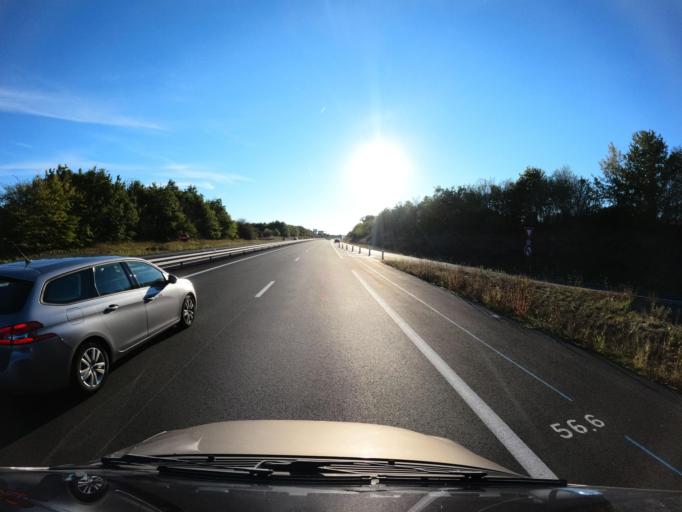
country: FR
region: Pays de la Loire
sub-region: Departement de Maine-et-Loire
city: La Tessoualle
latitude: 47.0159
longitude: -0.8783
